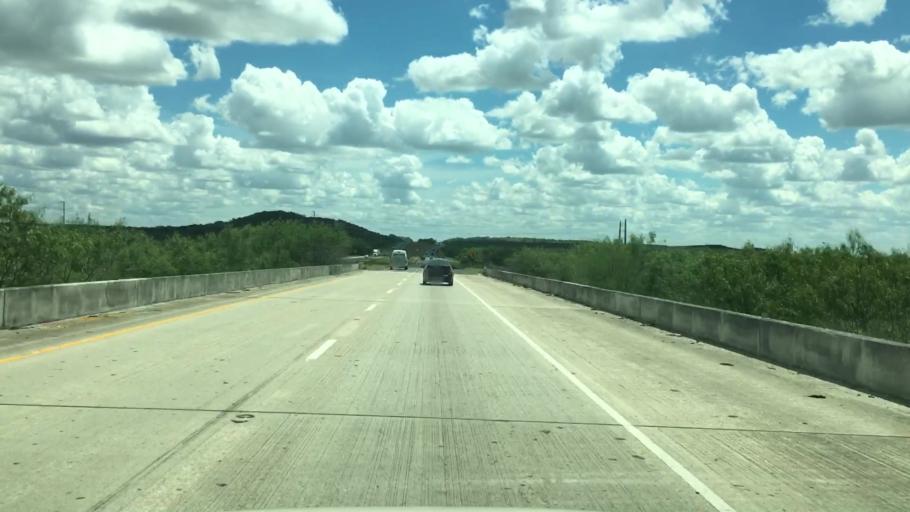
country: US
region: Texas
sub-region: Live Oak County
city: Three Rivers
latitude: 28.7315
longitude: -98.2886
